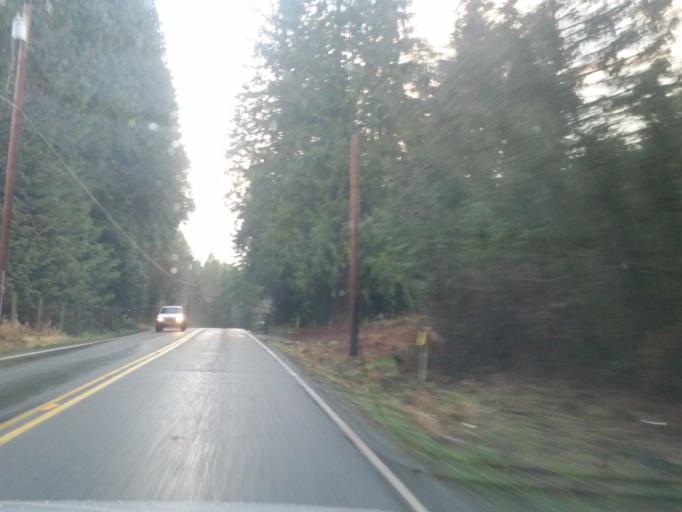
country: US
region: Washington
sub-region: Snohomish County
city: Maltby
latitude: 47.8184
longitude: -122.0930
